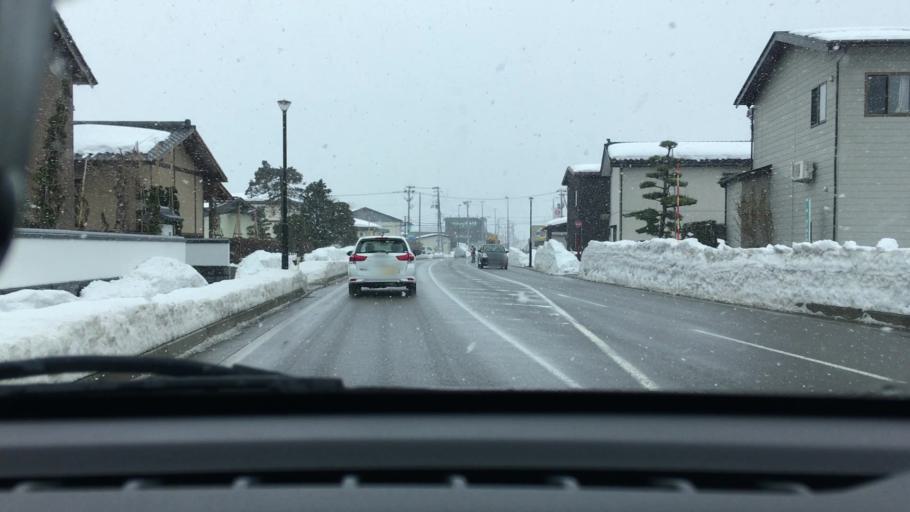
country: JP
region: Niigata
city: Joetsu
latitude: 37.1621
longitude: 138.2530
